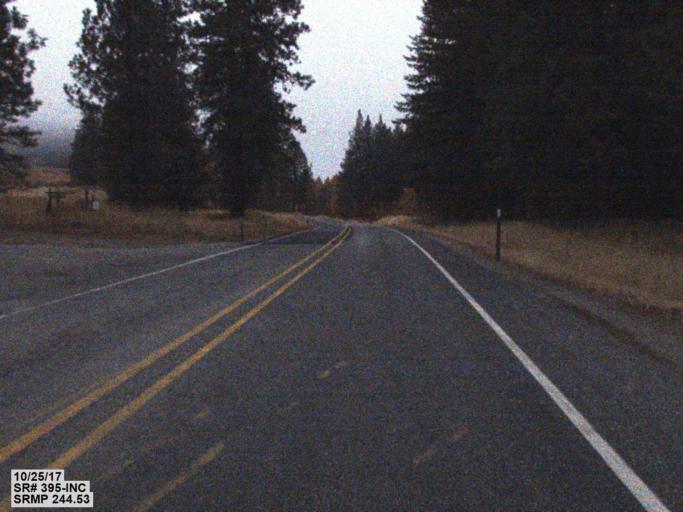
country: US
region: Washington
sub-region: Stevens County
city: Kettle Falls
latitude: 48.6636
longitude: -118.1140
